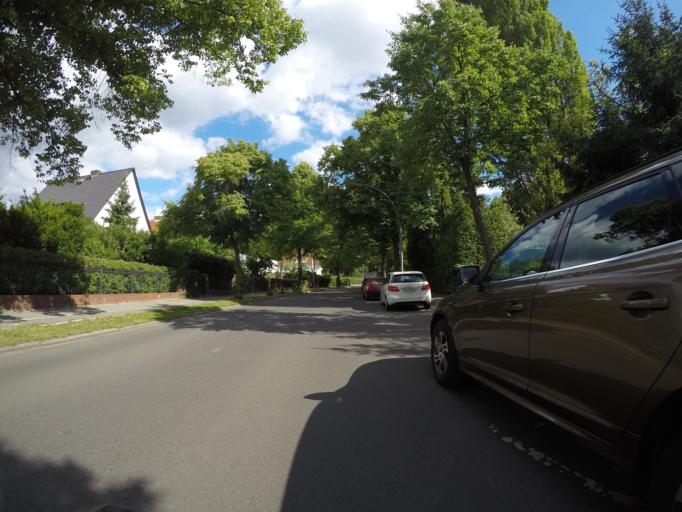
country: DE
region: Berlin
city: Zehlendorf Bezirk
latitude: 52.4443
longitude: 13.2694
